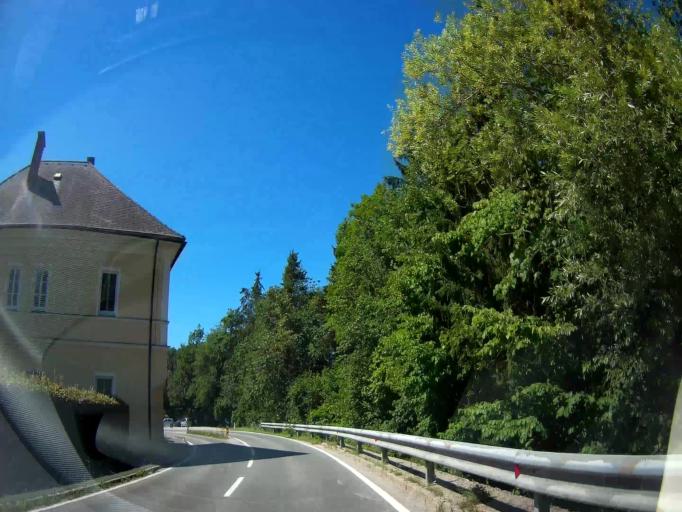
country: AT
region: Carinthia
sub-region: Politischer Bezirk Volkermarkt
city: Gallizien
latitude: 46.5580
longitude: 14.5100
